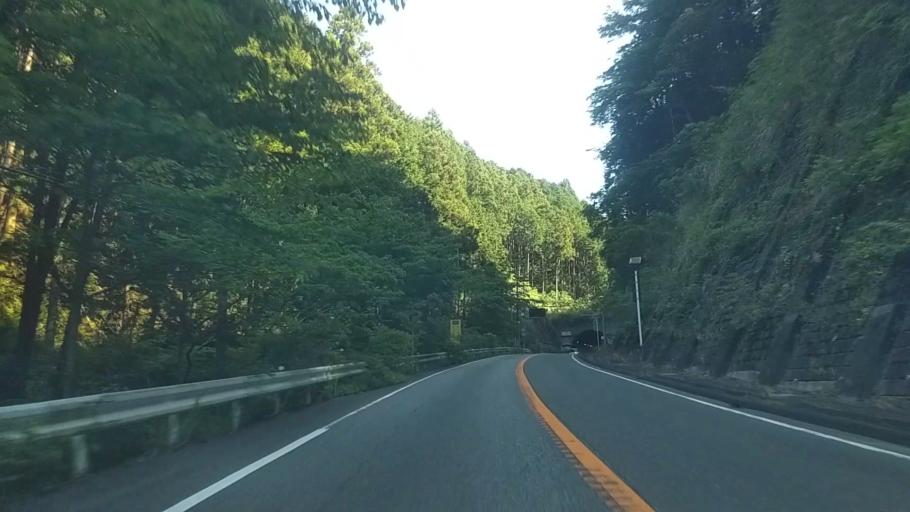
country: JP
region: Shizuoka
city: Fujinomiya
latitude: 35.2051
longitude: 138.5159
